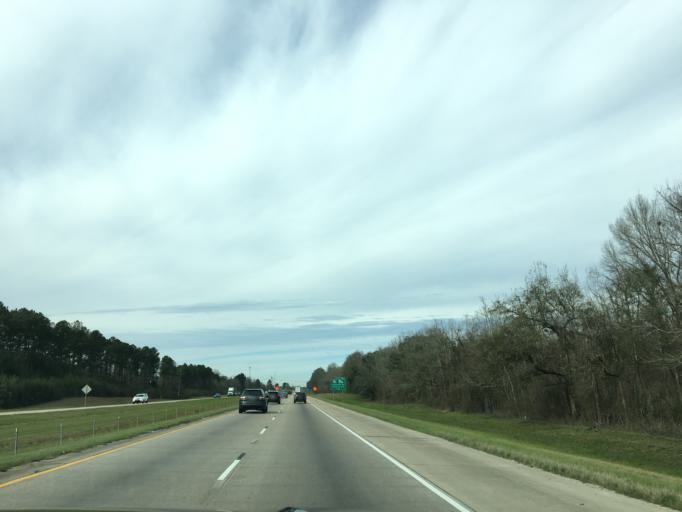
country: US
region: Louisiana
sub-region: Ascension Parish
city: Prairieville
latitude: 30.3311
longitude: -91.0147
